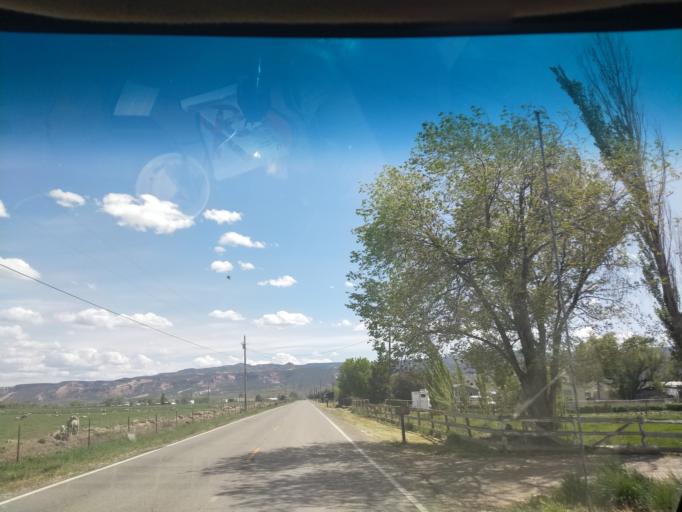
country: US
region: Colorado
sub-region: Mesa County
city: Fruita
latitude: 39.1747
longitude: -108.7571
